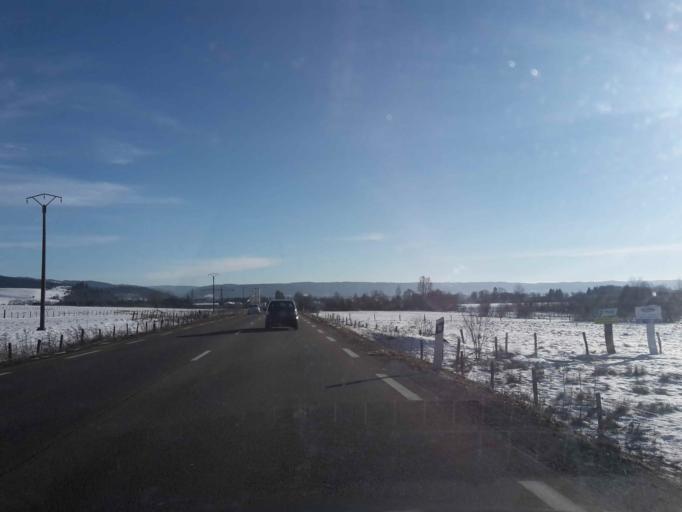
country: FR
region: Franche-Comte
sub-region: Departement du Doubs
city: Doubs
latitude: 46.9505
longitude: 6.3421
